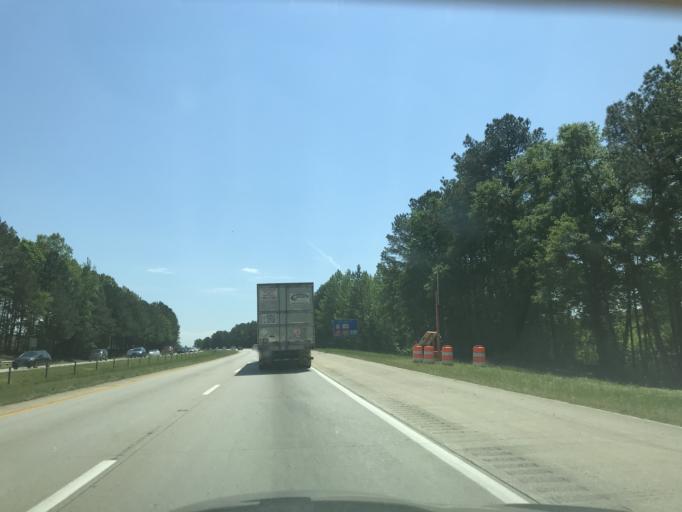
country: US
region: North Carolina
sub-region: Wake County
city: Garner
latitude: 35.6185
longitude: -78.5674
